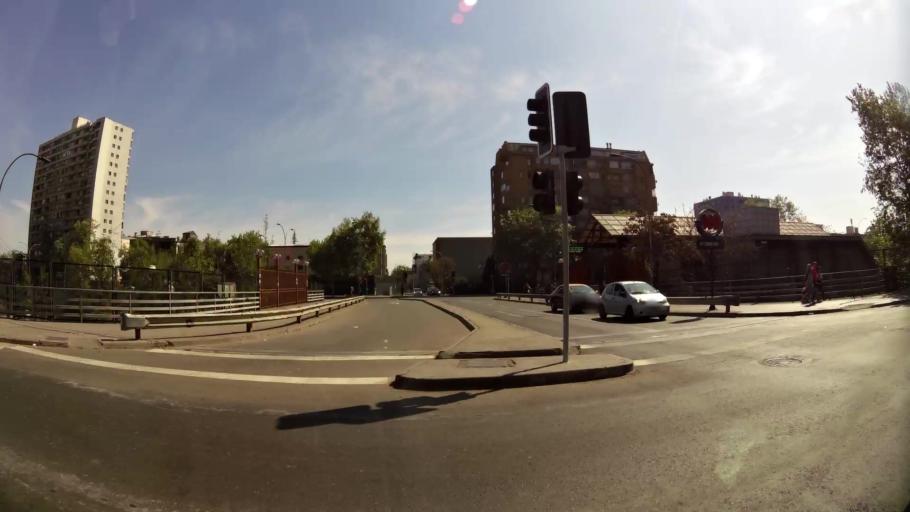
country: CL
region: Santiago Metropolitan
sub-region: Provincia de Santiago
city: Santiago
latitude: -33.4394
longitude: -70.6594
